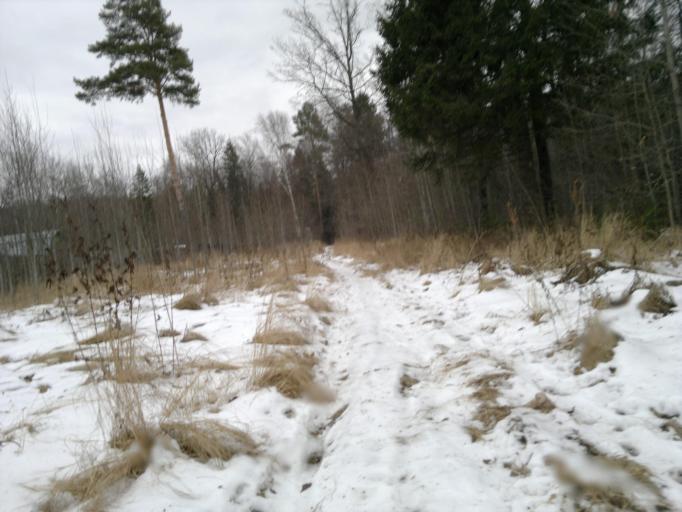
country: RU
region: Mariy-El
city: Yoshkar-Ola
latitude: 56.6102
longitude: 47.9543
